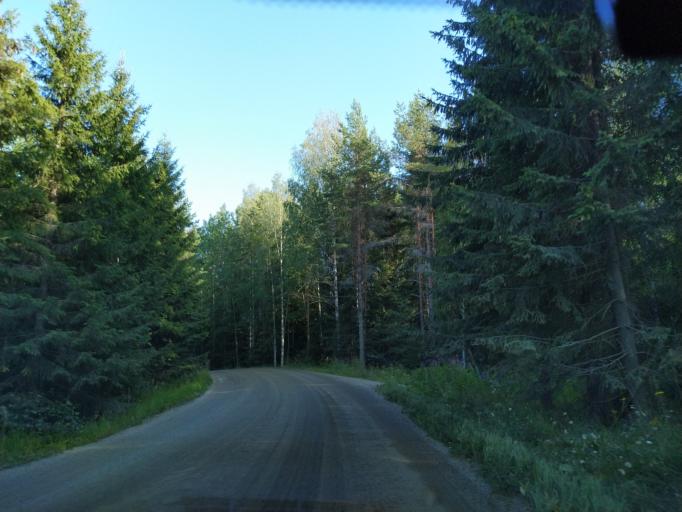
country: FI
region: Central Finland
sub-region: Jaemsae
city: Kuhmoinen
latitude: 61.6174
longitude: 25.1043
